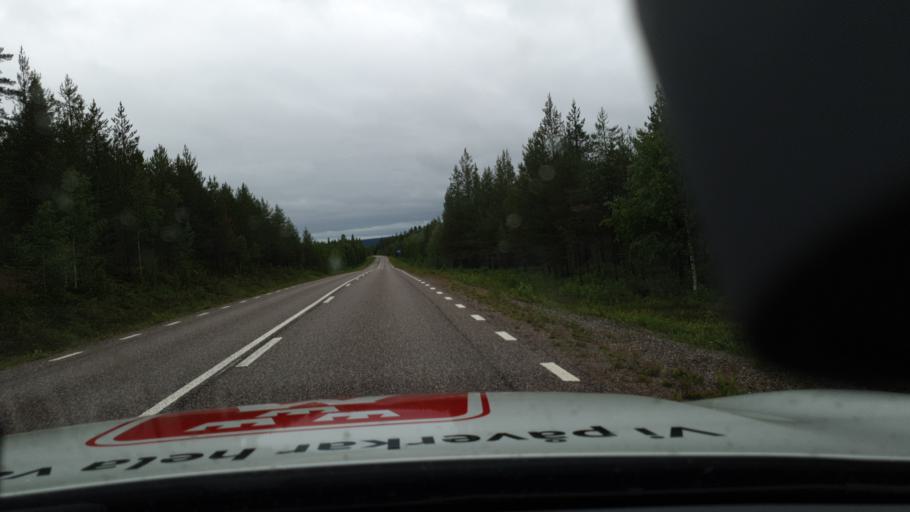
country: SE
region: Norrbotten
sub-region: Pajala Kommun
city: Pajala
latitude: 67.1785
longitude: 23.4990
